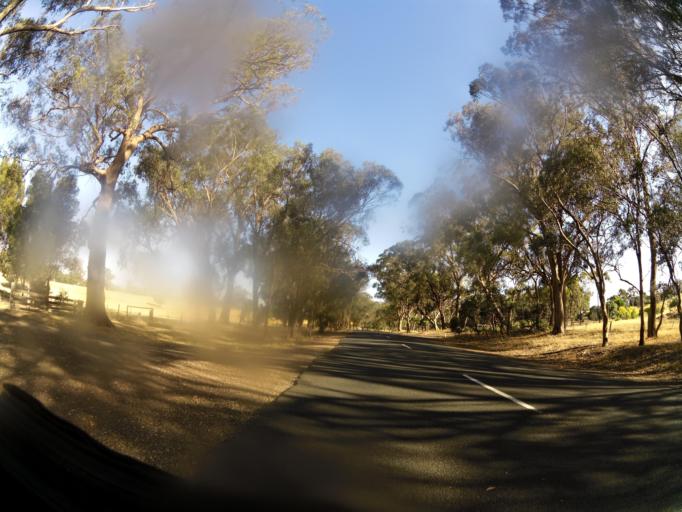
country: AU
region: Victoria
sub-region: Murrindindi
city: Kinglake West
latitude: -37.0058
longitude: 145.1227
